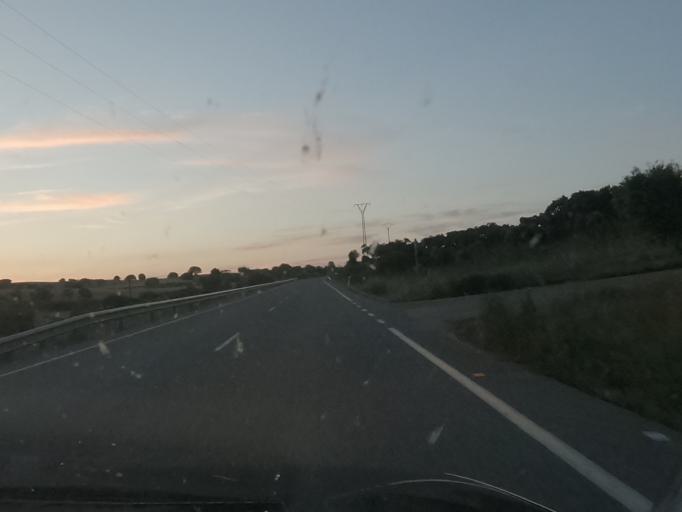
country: ES
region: Extremadura
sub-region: Provincia de Caceres
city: Piedras Albas
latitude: 39.7710
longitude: -6.9154
